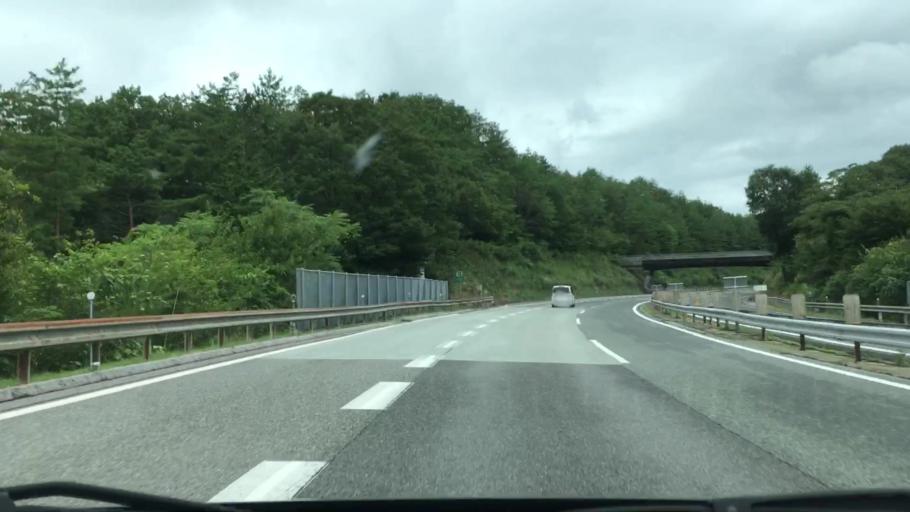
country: JP
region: Hiroshima
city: Miyoshi
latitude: 34.7529
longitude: 132.7632
